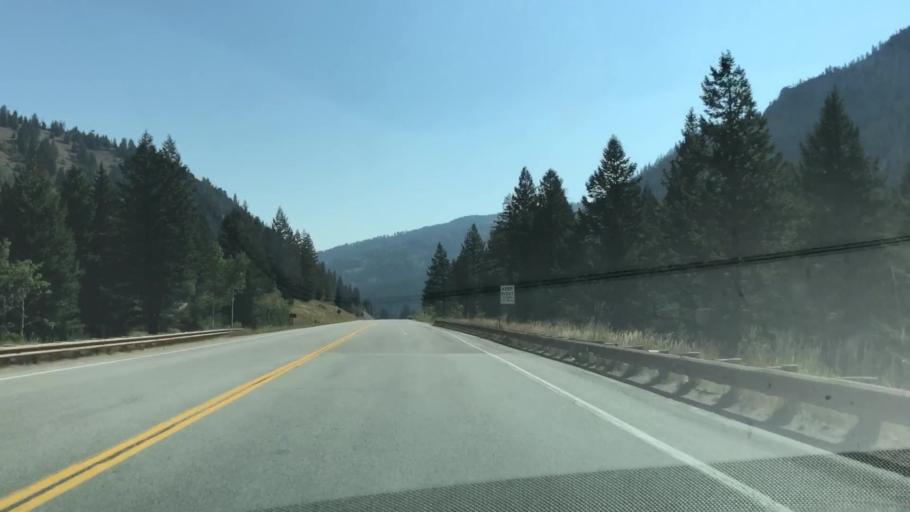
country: US
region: Wyoming
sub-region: Teton County
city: Hoback
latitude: 43.1981
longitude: -110.9014
